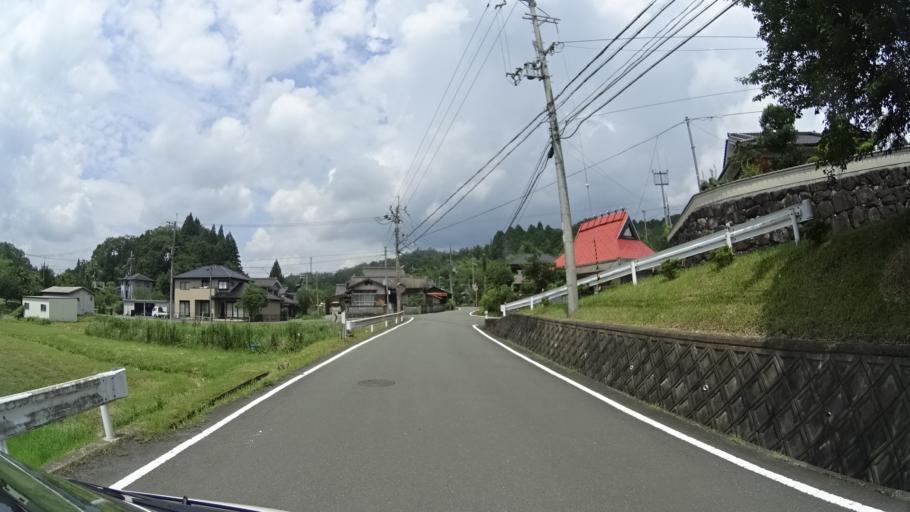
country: JP
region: Kyoto
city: Ayabe
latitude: 35.1785
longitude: 135.3607
